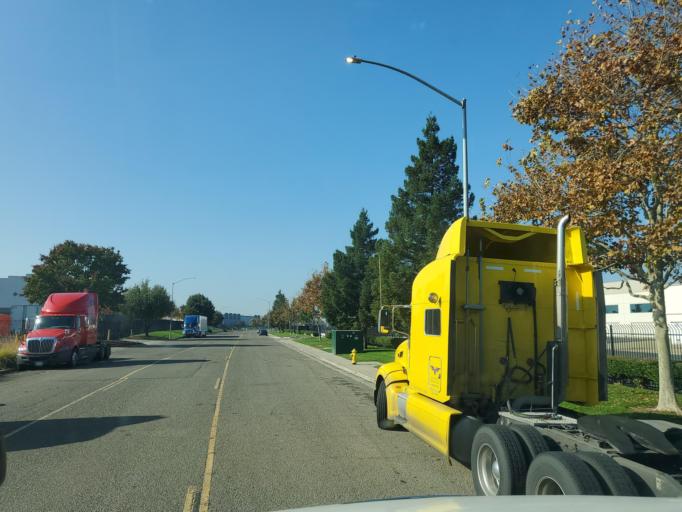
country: US
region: California
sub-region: San Joaquin County
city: Kennedy
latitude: 37.9086
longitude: -121.2465
